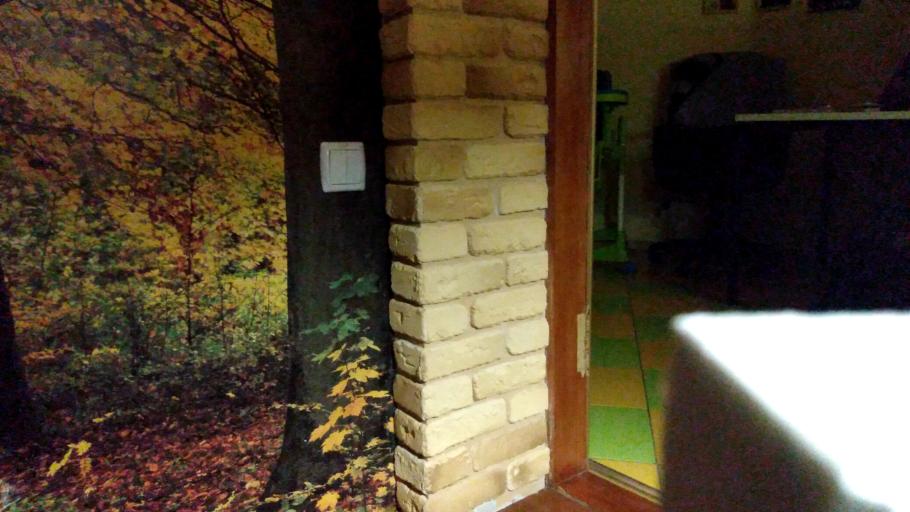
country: RU
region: Vologda
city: Lipin Bor
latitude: 60.8450
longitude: 38.0168
